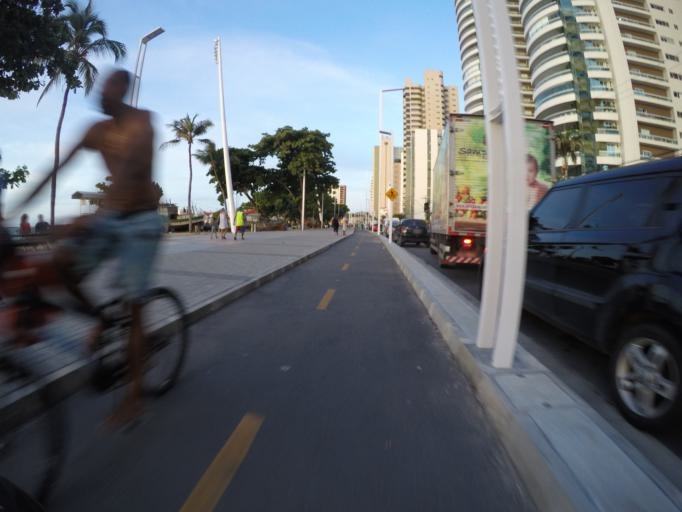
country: BR
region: Ceara
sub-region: Fortaleza
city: Fortaleza
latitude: -3.7227
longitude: -38.4826
